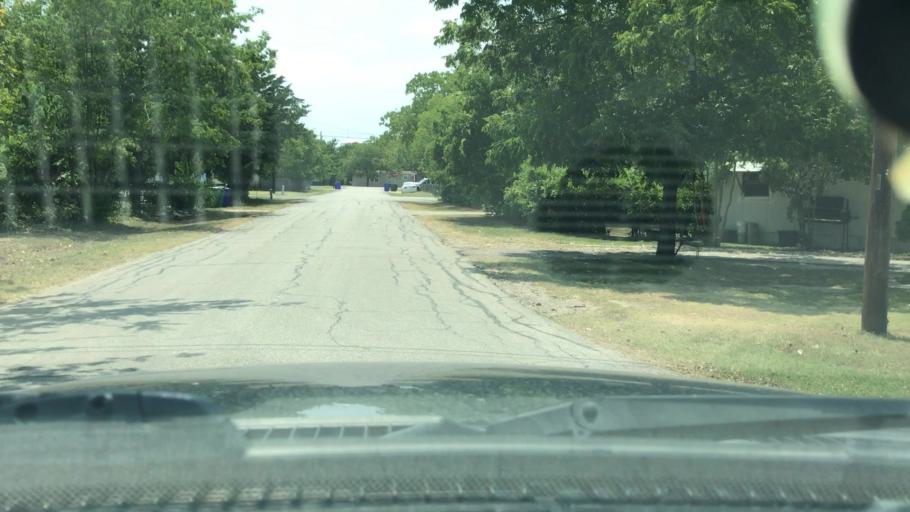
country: US
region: Texas
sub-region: Williamson County
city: Cedar Park
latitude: 30.5353
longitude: -97.8388
